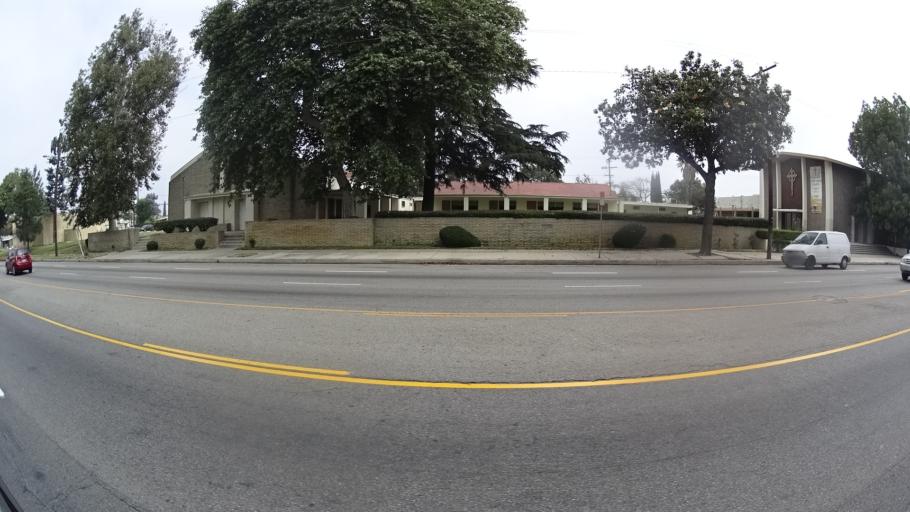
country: US
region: California
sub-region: Los Angeles County
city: Van Nuys
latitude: 34.2216
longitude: -118.4424
